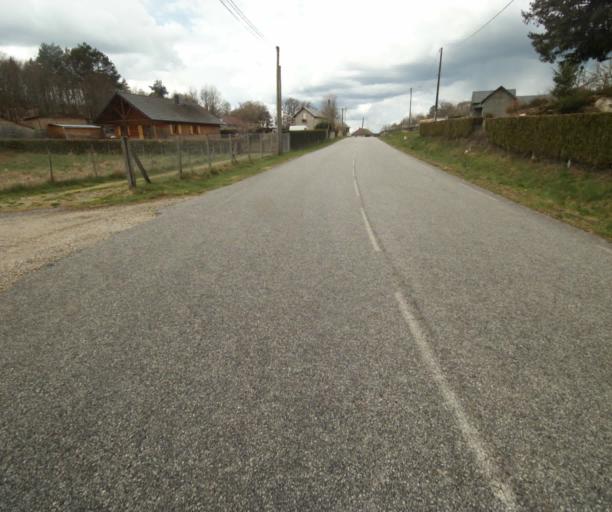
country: FR
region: Limousin
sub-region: Departement de la Correze
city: Correze
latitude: 45.3351
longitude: 1.9408
